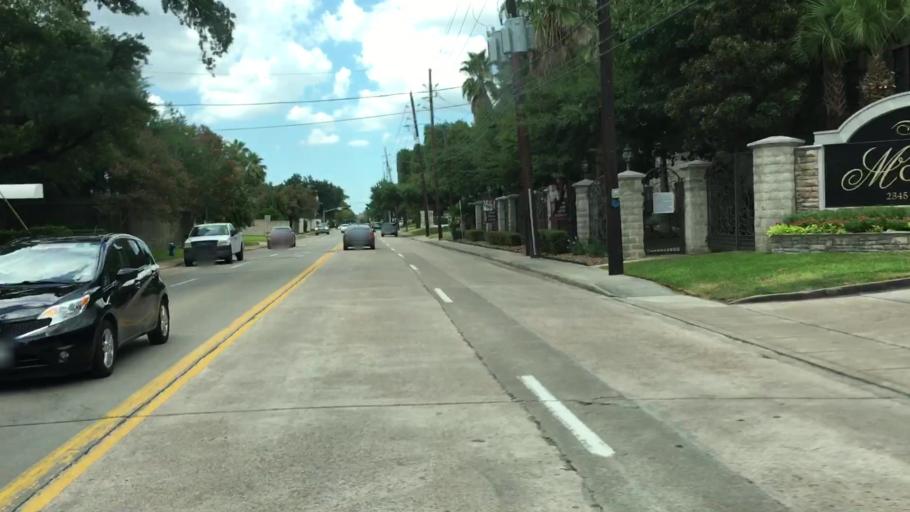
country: US
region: Texas
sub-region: Harris County
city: Bellaire
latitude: 29.7439
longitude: -95.4670
